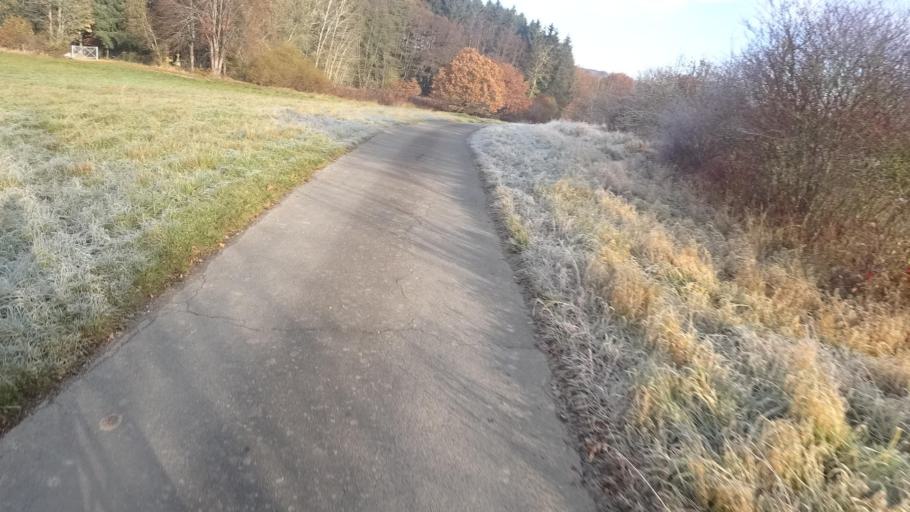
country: DE
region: Rheinland-Pfalz
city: Hausbay
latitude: 50.1133
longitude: 7.5590
